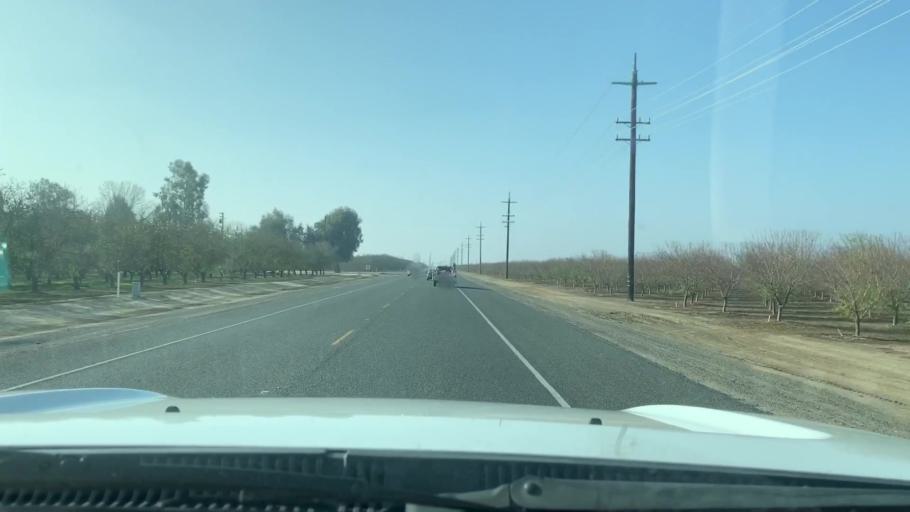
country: US
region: California
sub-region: Kern County
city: Wasco
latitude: 35.6014
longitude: -119.4220
